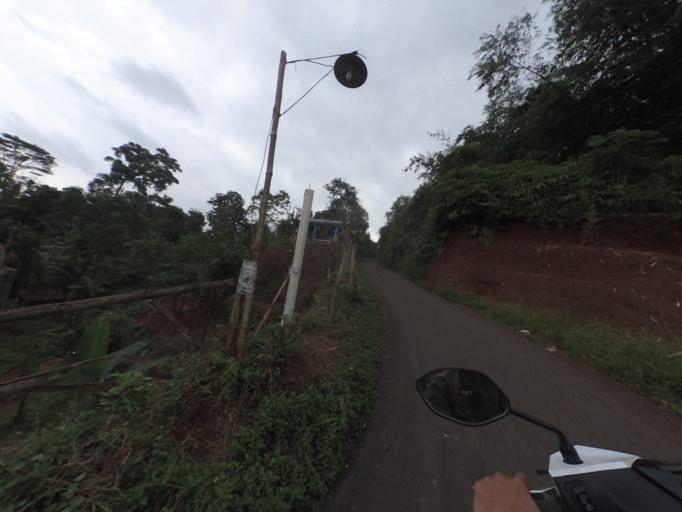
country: ID
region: West Java
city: Ciampea
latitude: -6.5989
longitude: 106.7233
